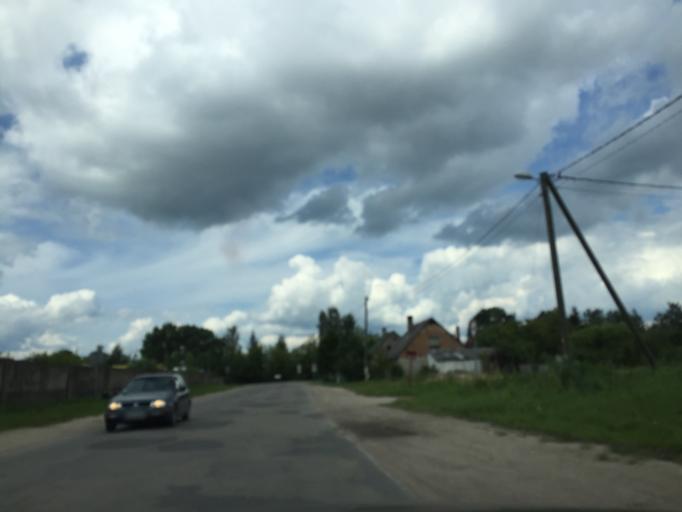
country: LV
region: Jelgava
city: Jelgava
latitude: 56.6290
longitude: 23.7055
